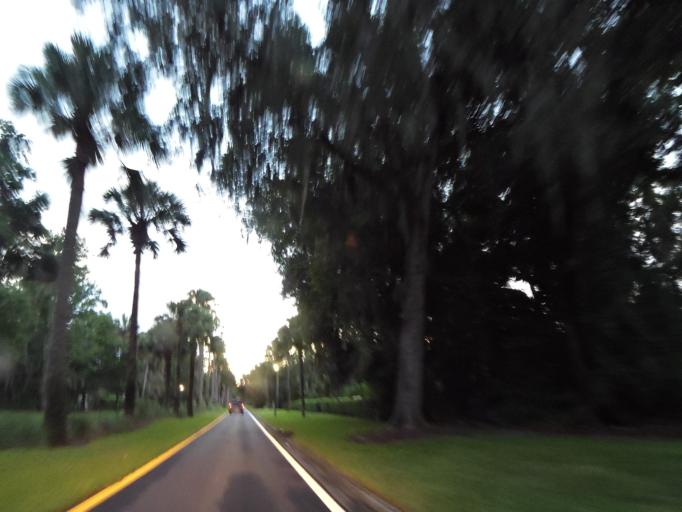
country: US
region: Florida
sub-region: Duval County
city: Jacksonville
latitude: 30.3822
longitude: -81.6168
